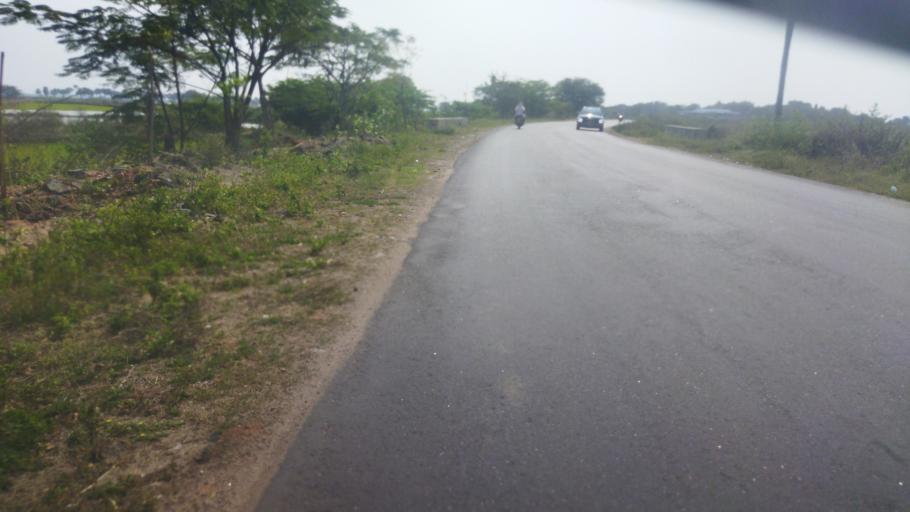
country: IN
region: Telangana
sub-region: Nalgonda
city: Nalgonda
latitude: 17.0990
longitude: 79.2854
